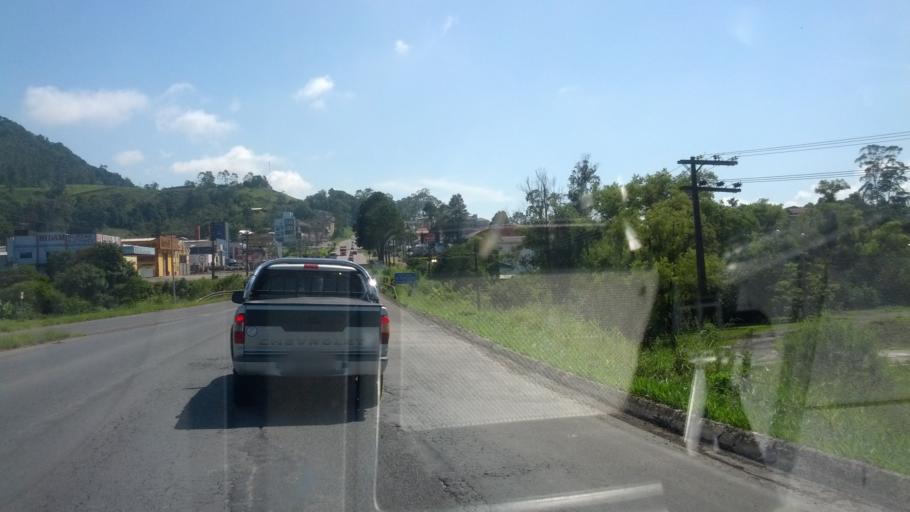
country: BR
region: Santa Catarina
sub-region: Rio Do Sul
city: Rio do Sul
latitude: -27.2090
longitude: -49.6514
